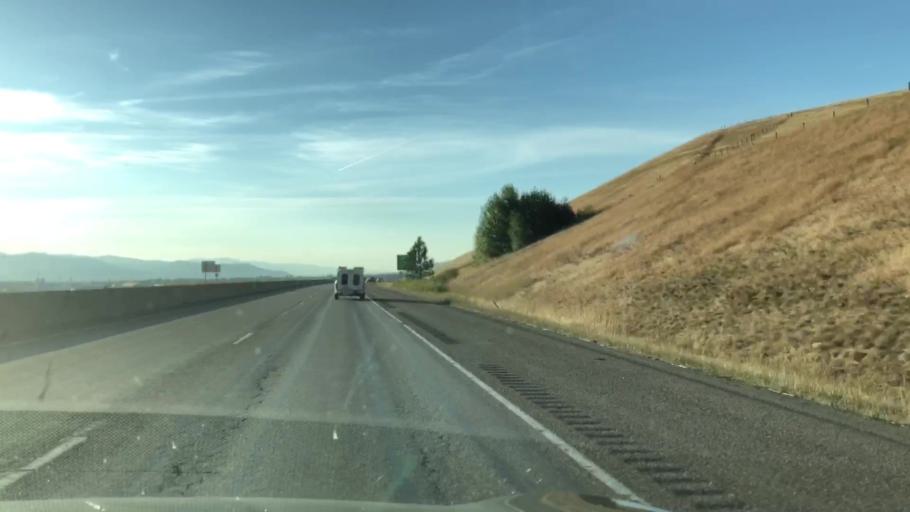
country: US
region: Montana
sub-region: Missoula County
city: Missoula
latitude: 46.8930
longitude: -114.0055
